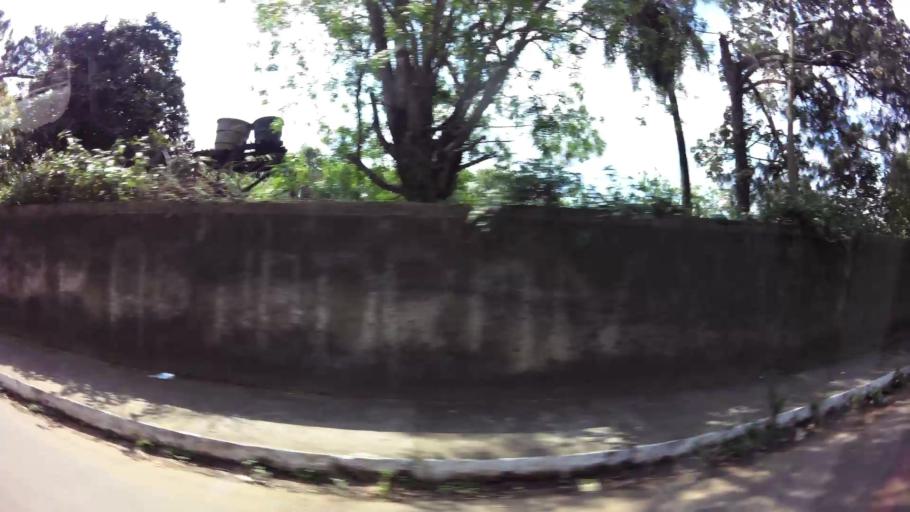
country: PY
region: Central
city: San Lorenzo
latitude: -25.3377
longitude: -57.5032
